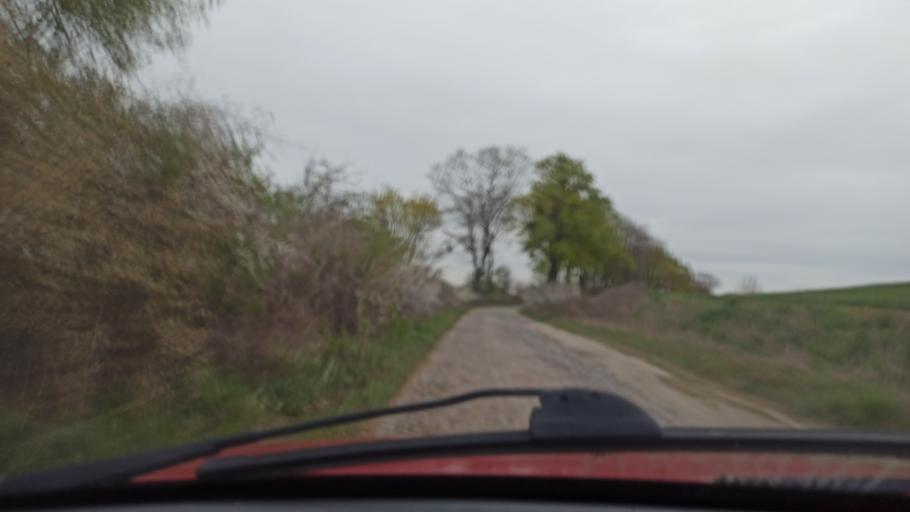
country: PL
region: Kujawsko-Pomorskie
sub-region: Powiat grudziadzki
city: Lasin
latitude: 53.5678
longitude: 19.0778
